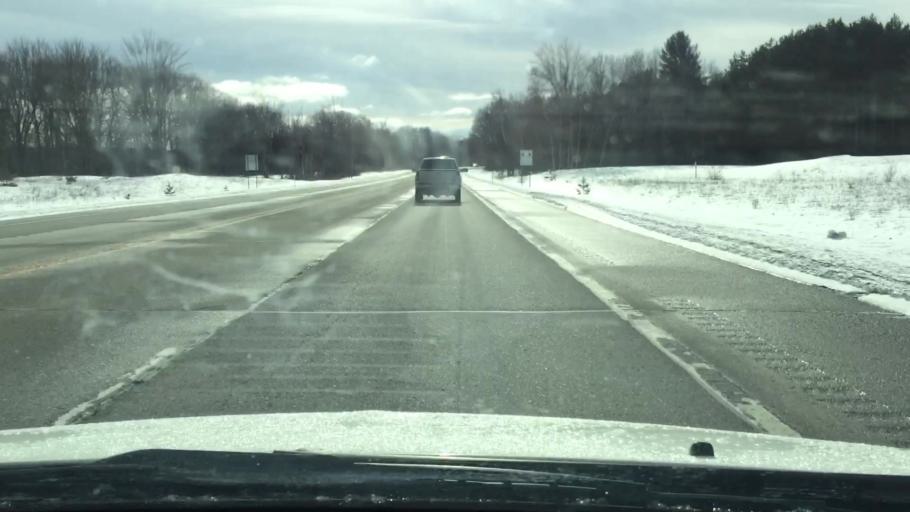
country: US
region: Michigan
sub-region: Kalkaska County
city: Kalkaska
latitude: 44.6182
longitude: -85.3023
